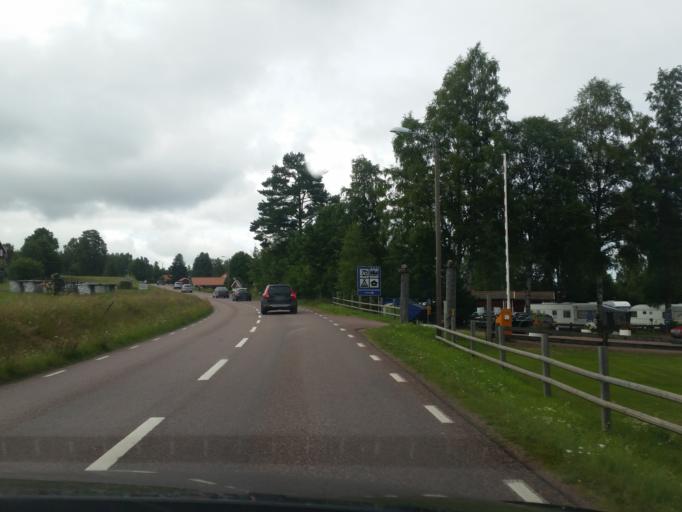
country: SE
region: Dalarna
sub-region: Leksand Municipality
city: Leksand
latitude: 60.7299
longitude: 14.9515
